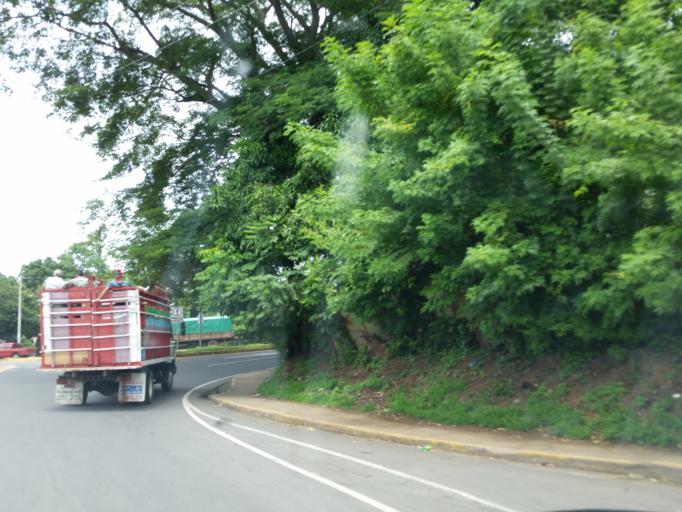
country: NI
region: Masaya
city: Masaya
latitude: 11.9742
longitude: -86.0755
